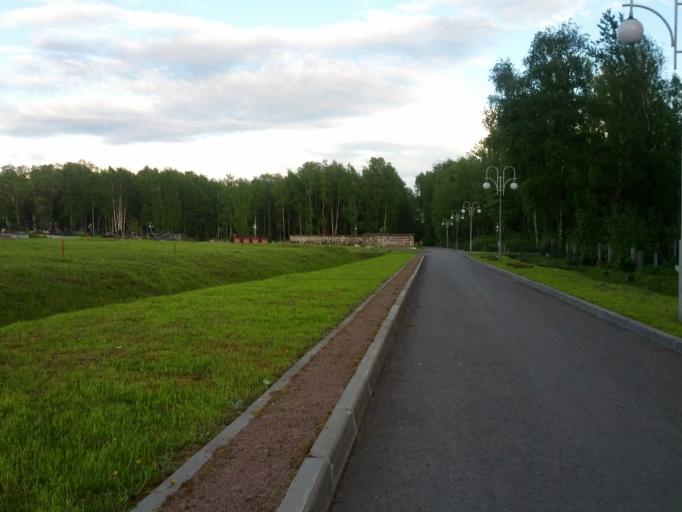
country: RU
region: St.-Petersburg
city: Centralniy
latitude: 59.9135
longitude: 30.4293
